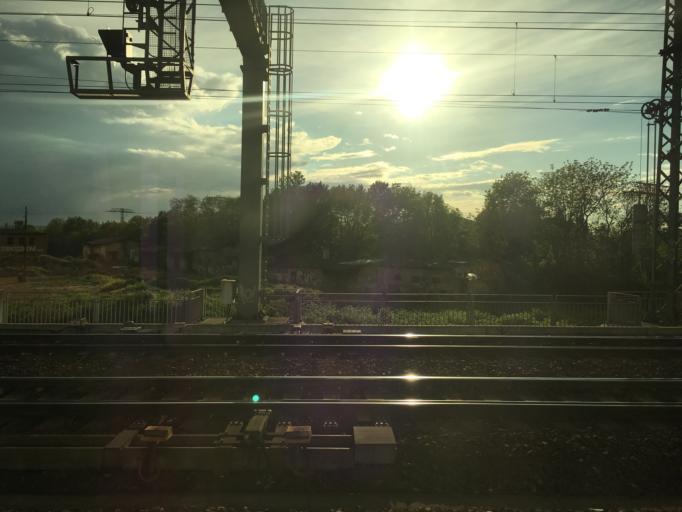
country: DE
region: Saxony
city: Dresden
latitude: 51.0498
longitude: 13.7193
